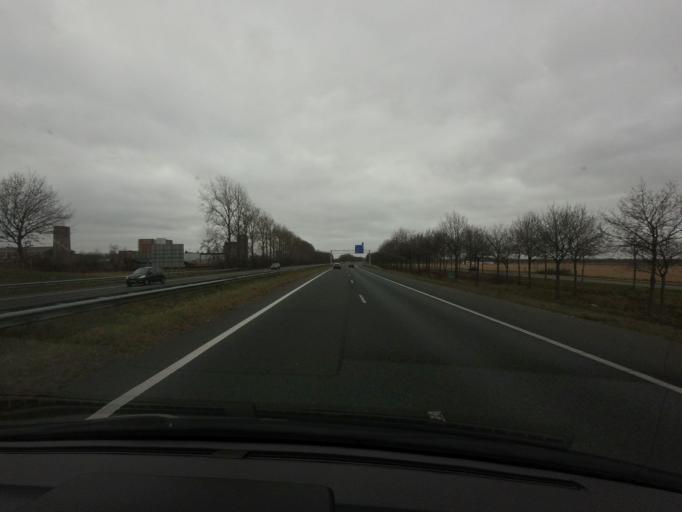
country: NL
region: Groningen
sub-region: Gemeente Hoogezand-Sappemeer
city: Hoogezand
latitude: 53.1688
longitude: 6.7698
